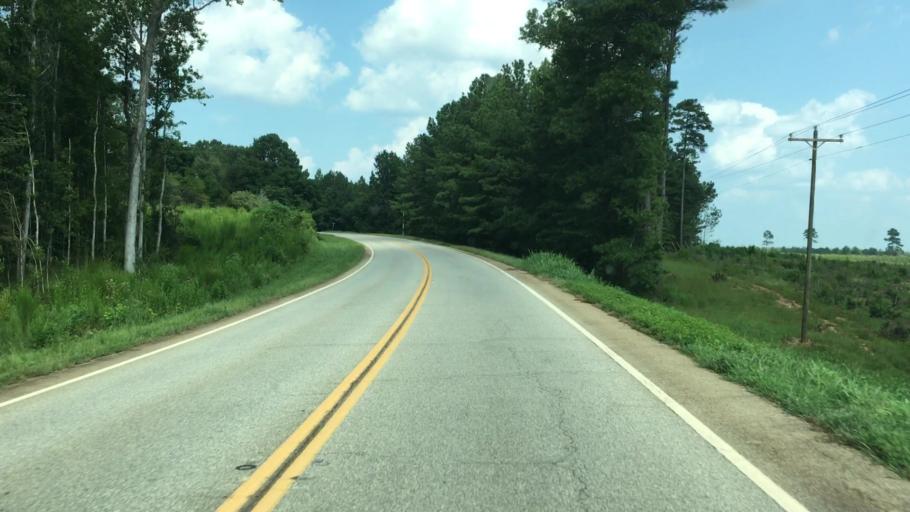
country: US
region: Georgia
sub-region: Monroe County
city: Forsyth
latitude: 33.1029
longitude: -83.8791
